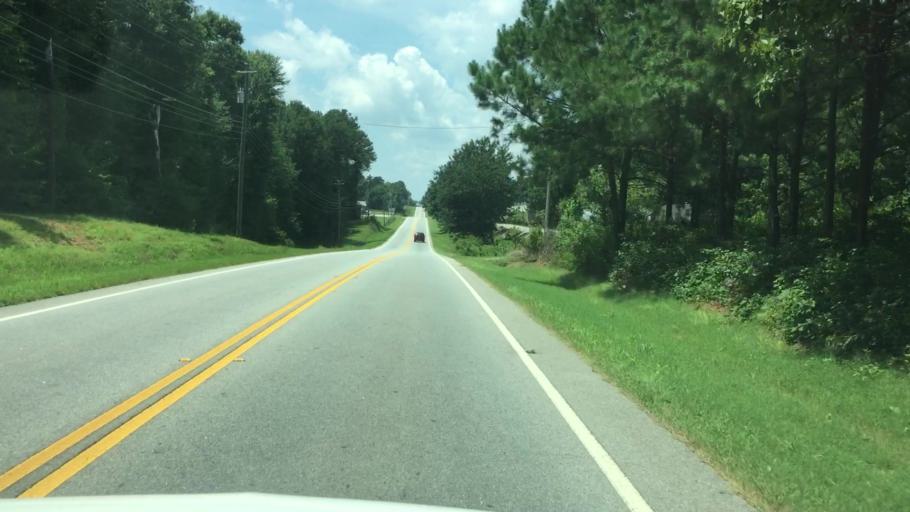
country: US
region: Georgia
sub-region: Barrow County
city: Auburn
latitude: 33.9948
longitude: -83.7867
